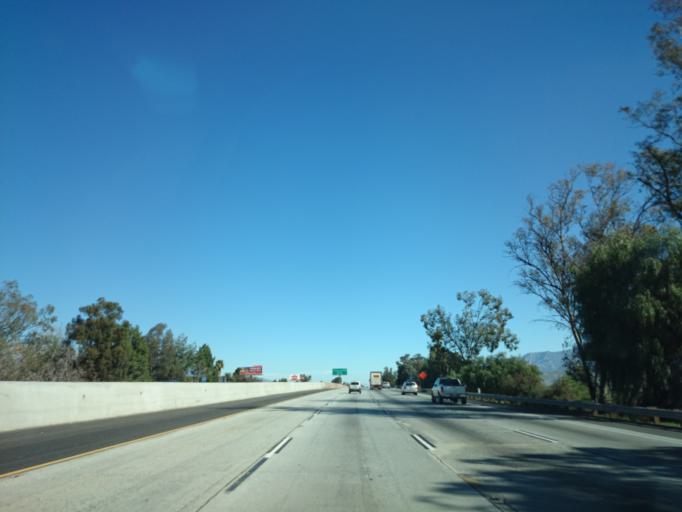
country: US
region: California
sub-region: Riverside County
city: Beaumont
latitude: 33.9272
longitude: -116.9682
